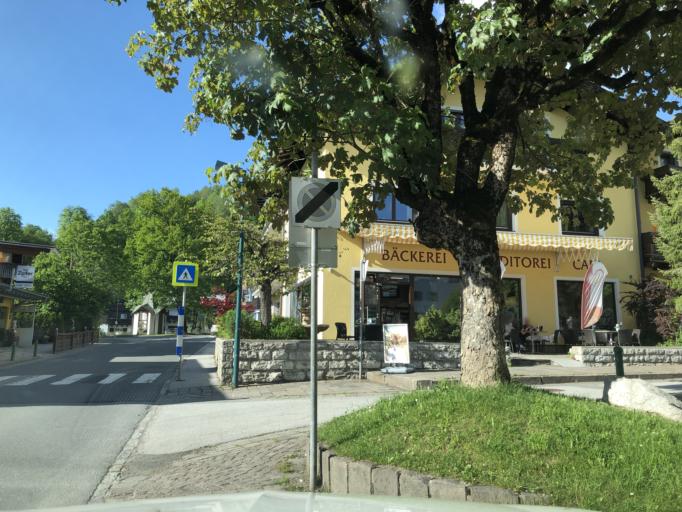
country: AT
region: Salzburg
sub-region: Politischer Bezirk Zell am See
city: Zell am See
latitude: 47.3291
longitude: 12.8169
